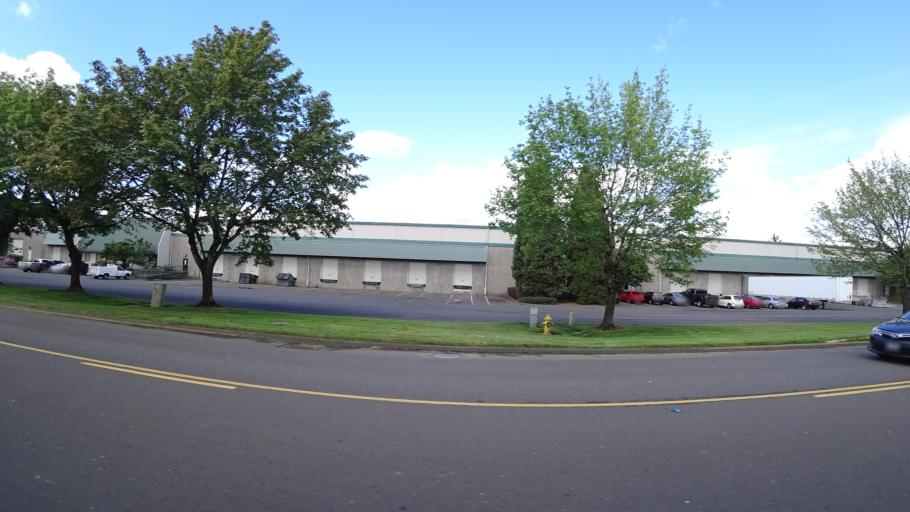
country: US
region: Oregon
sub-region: Washington County
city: Durham
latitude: 45.4069
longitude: -122.7490
